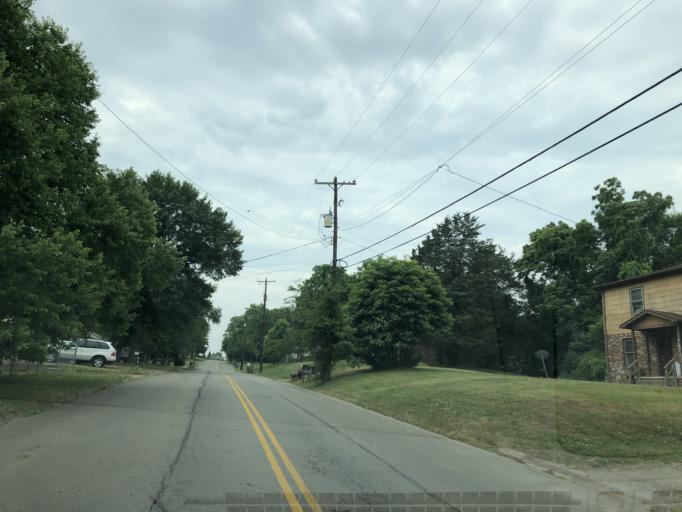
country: US
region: Tennessee
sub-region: Davidson County
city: Oak Hill
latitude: 36.0758
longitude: -86.6897
